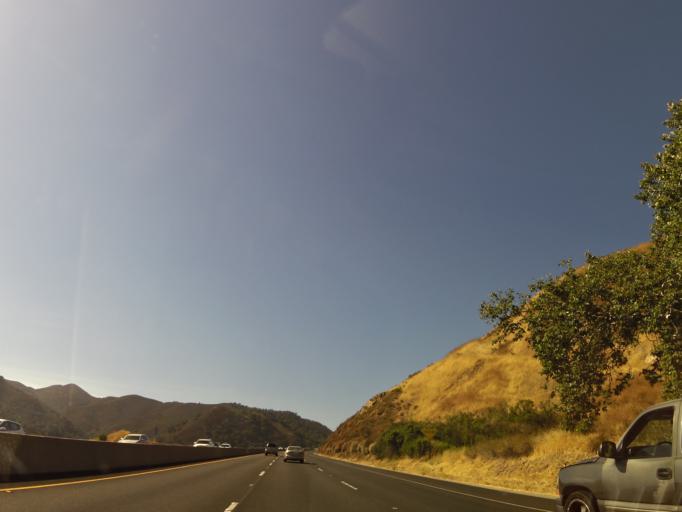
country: US
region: California
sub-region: San Luis Obispo County
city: Santa Margarita
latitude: 35.3349
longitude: -120.6252
